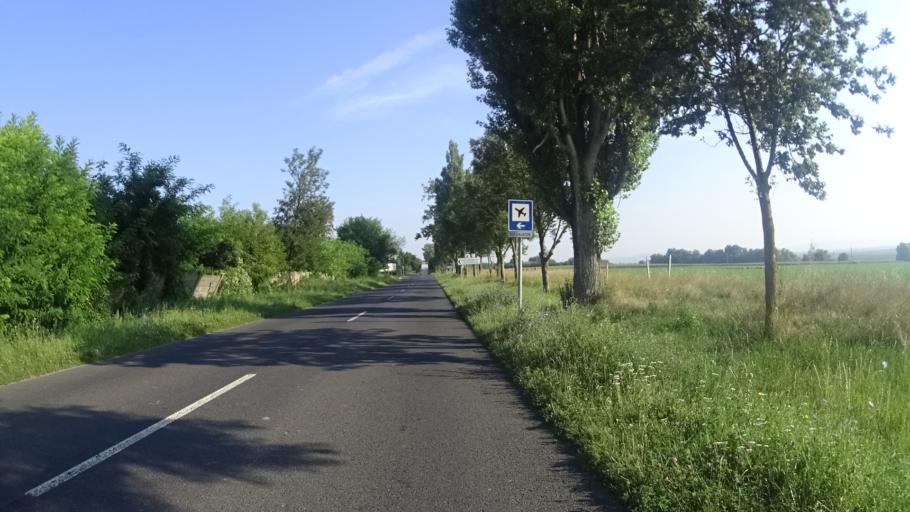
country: HU
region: Zala
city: Sarmellek
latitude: 46.6889
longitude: 17.1685
